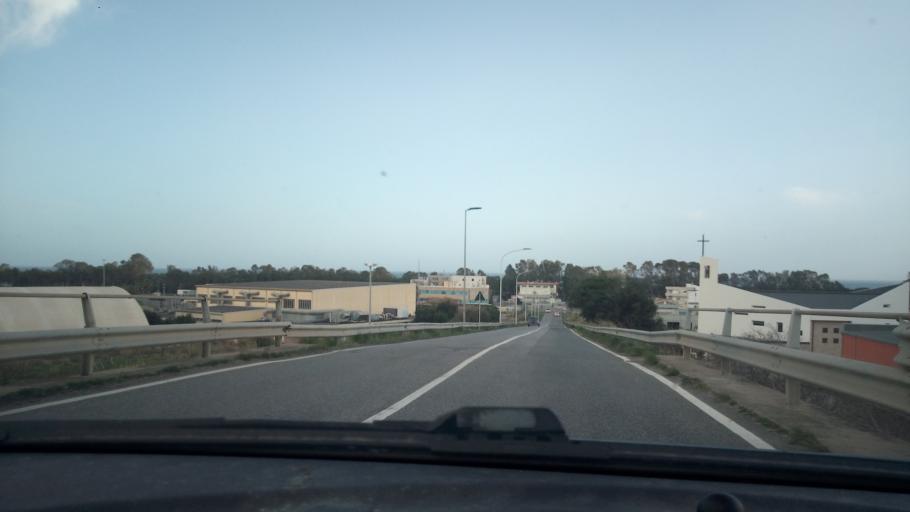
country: IT
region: Calabria
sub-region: Provincia di Catanzaro
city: Barone
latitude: 38.8339
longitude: 16.6376
